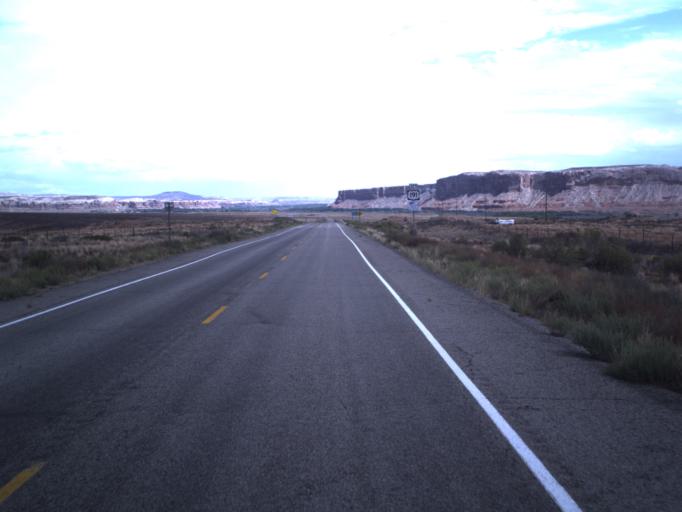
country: US
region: Utah
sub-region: San Juan County
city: Blanding
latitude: 37.2650
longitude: -109.6313
